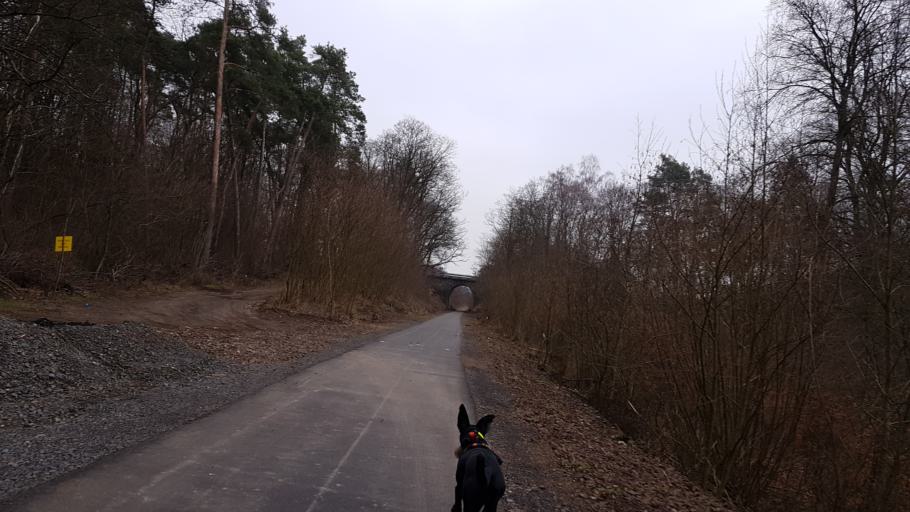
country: PL
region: West Pomeranian Voivodeship
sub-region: Powiat mysliborski
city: Barlinek
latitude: 53.0136
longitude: 15.2621
